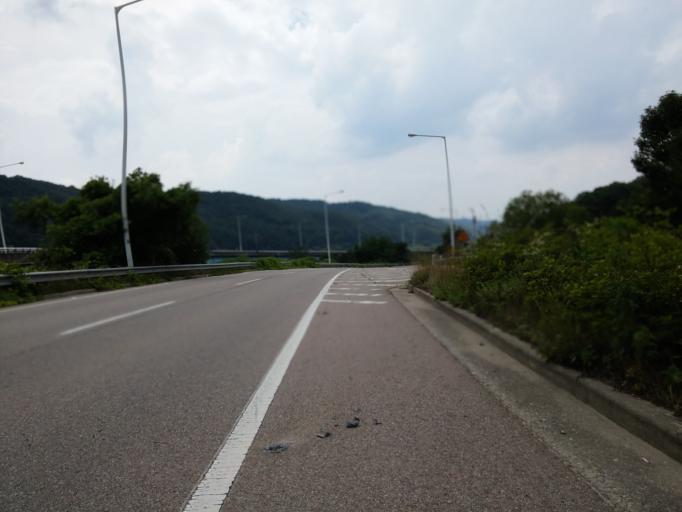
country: KR
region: Chungcheongnam-do
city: Gongju
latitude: 36.4415
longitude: 127.2036
